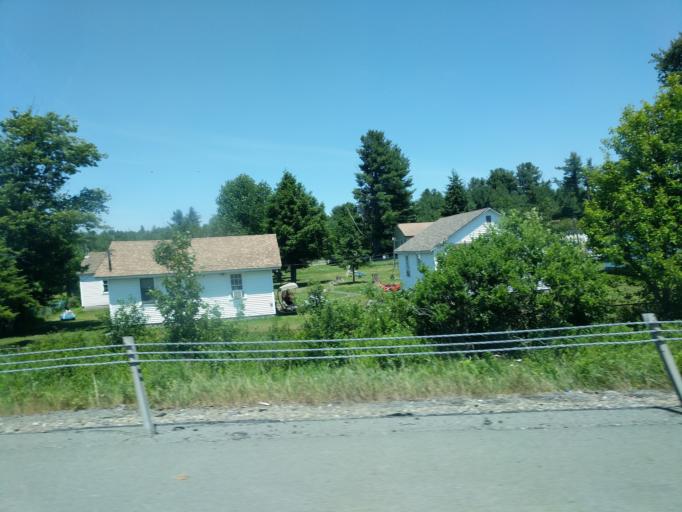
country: US
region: New York
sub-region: Sullivan County
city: Monticello
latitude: 41.6728
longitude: -74.7127
